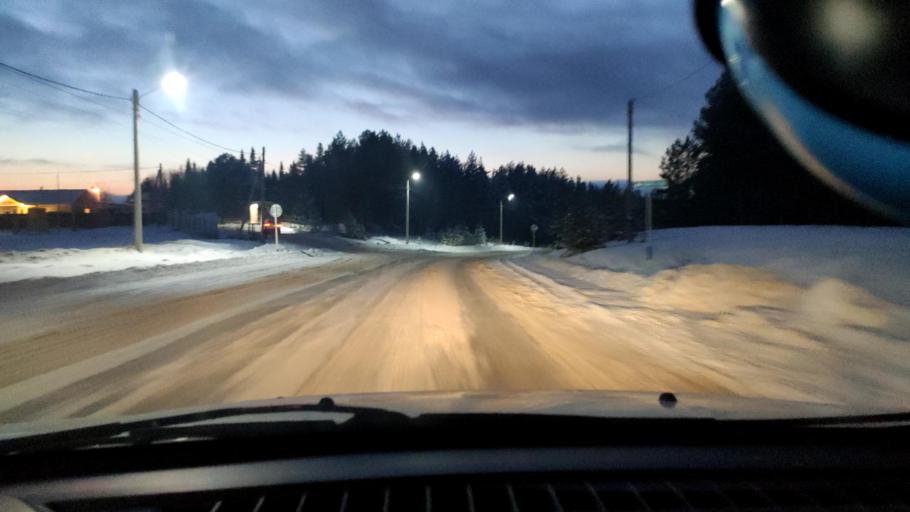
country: RU
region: Perm
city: Kultayevo
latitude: 57.9122
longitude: 55.9076
